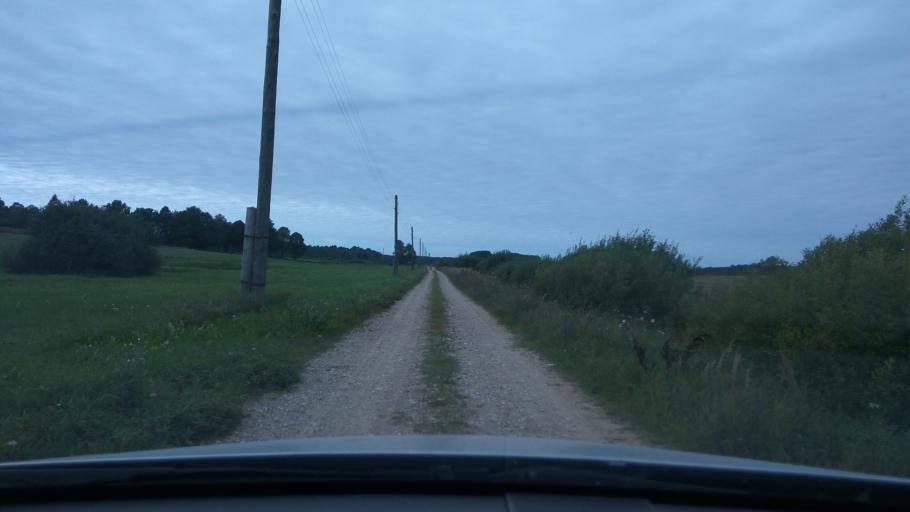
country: LV
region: Kuldigas Rajons
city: Kuldiga
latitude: 57.2416
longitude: 21.9555
